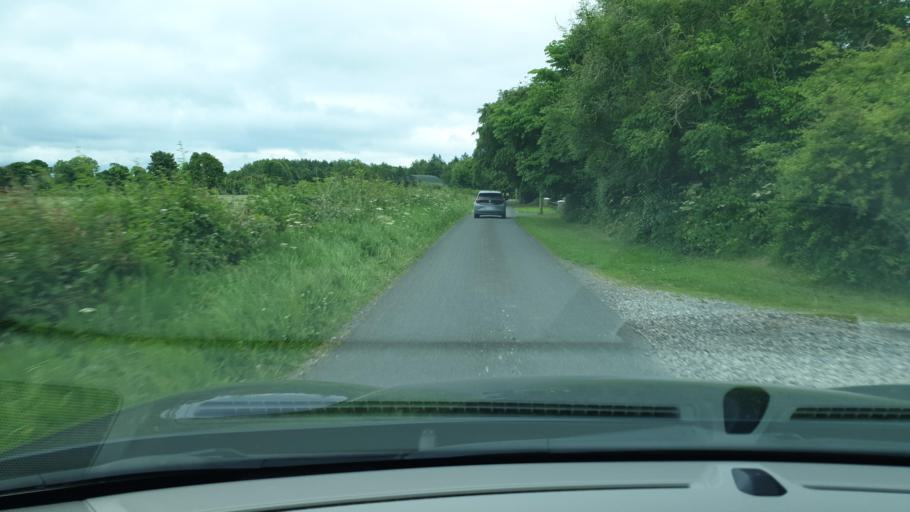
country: IE
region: Leinster
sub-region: An Mhi
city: Dunshaughlin
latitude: 53.5350
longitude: -6.5246
